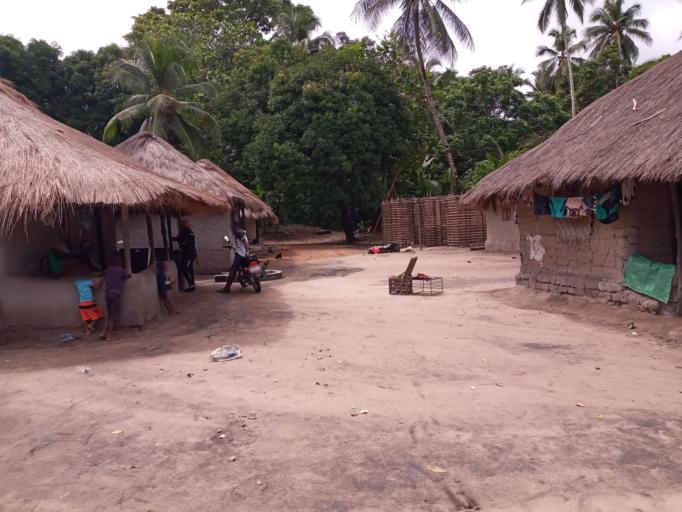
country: SL
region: Southern Province
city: Bonthe
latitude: 7.5241
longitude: -12.5749
